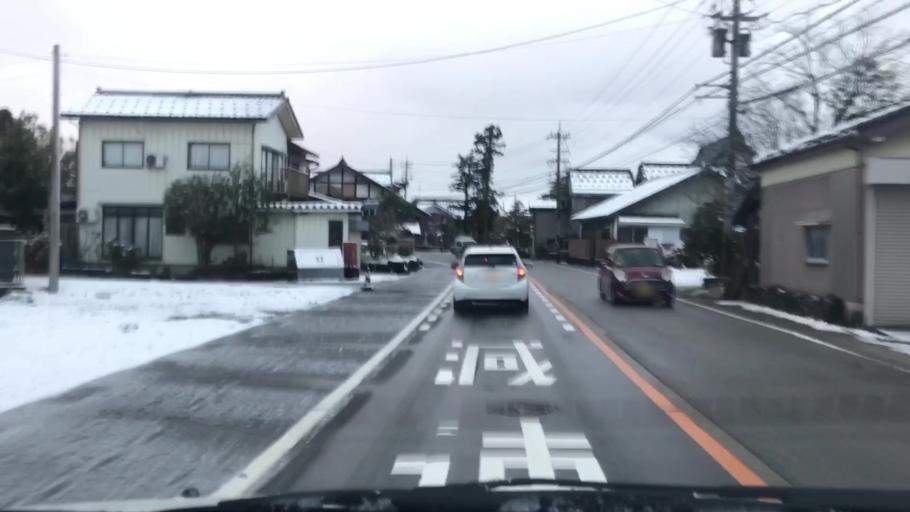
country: JP
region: Toyama
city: Kamiichi
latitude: 36.7011
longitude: 137.3277
